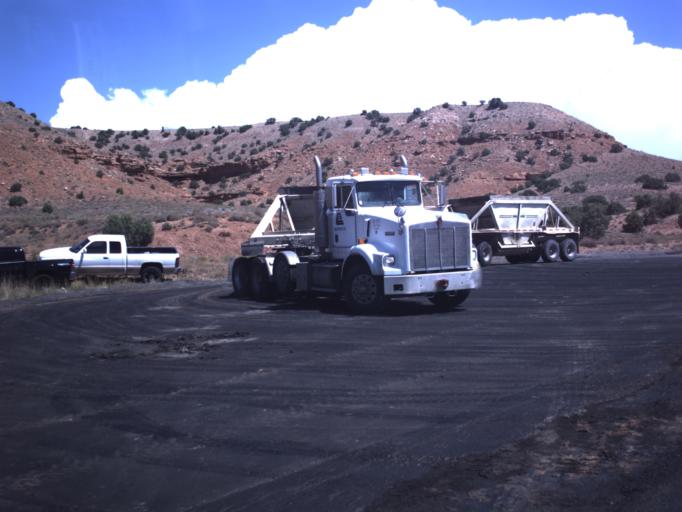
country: US
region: Utah
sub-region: Uintah County
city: Maeser
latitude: 40.4186
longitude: -109.6754
